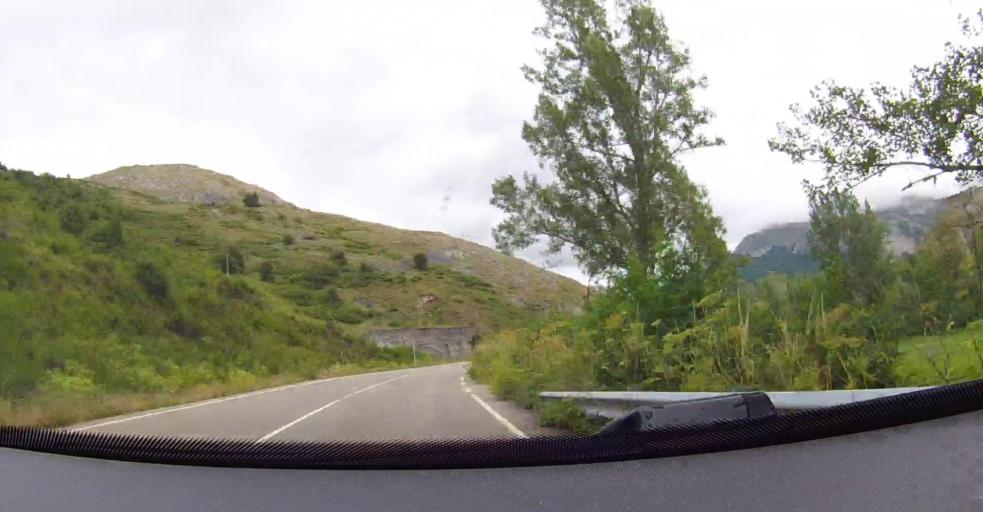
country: ES
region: Castille and Leon
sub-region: Provincia de Leon
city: Buron
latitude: 43.0281
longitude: -5.0655
